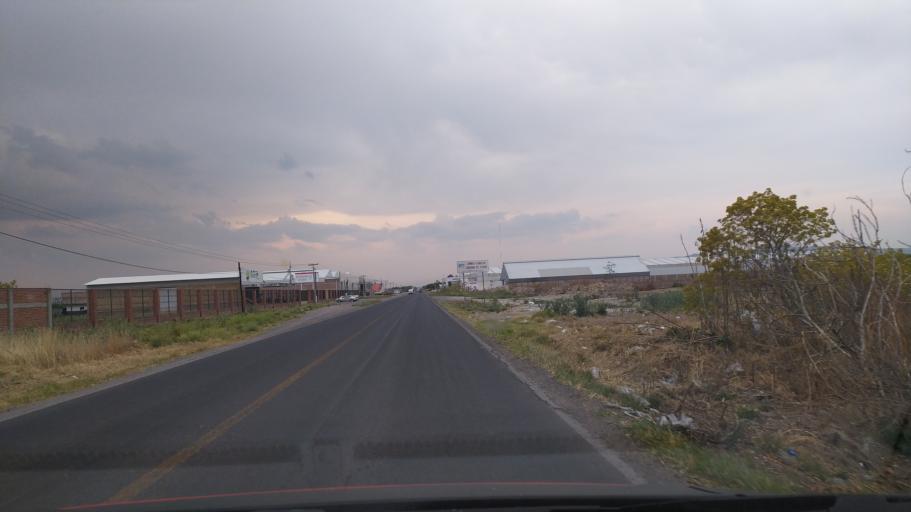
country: MX
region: Guanajuato
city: Ciudad Manuel Doblado
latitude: 20.7434
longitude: -101.9296
